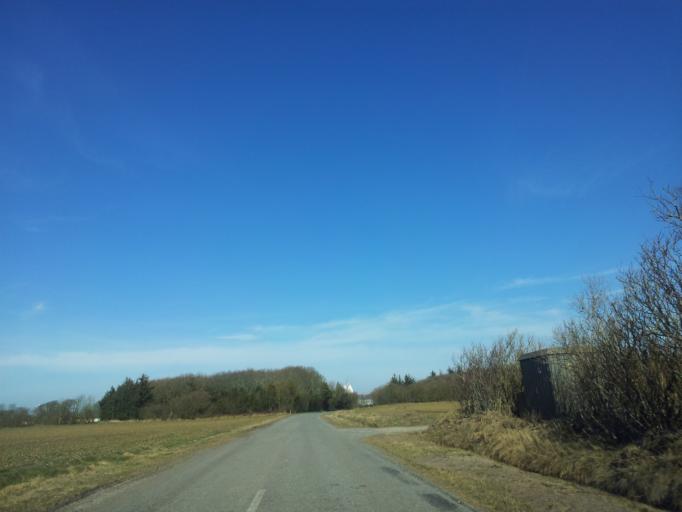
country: DK
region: South Denmark
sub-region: Tonder Kommune
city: Sherrebek
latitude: 55.1884
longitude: 8.7196
